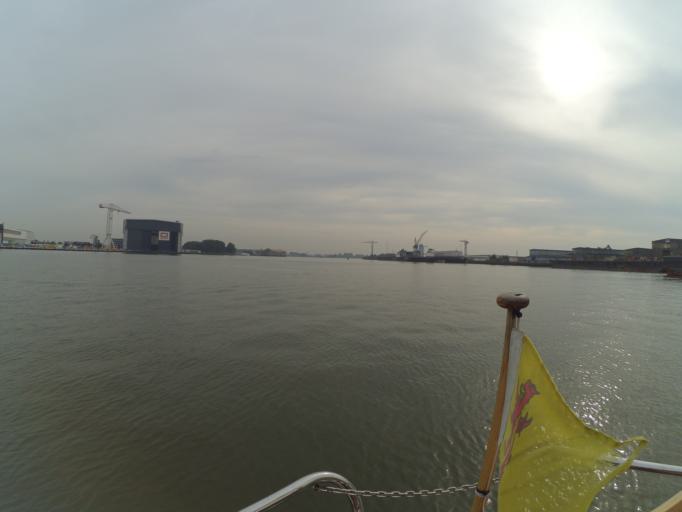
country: NL
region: South Holland
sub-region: Gemeente Capelle aan den IJssel
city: Capelle-West
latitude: 51.9035
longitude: 4.5644
